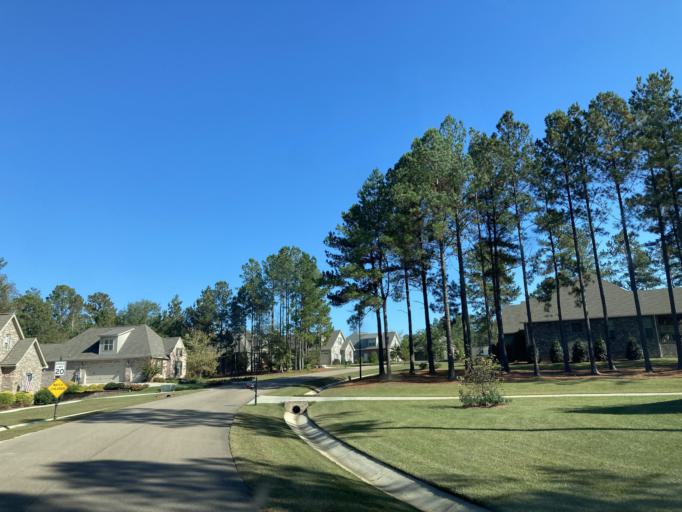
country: US
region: Mississippi
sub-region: Lamar County
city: Sumrall
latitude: 31.3300
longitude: -89.4885
